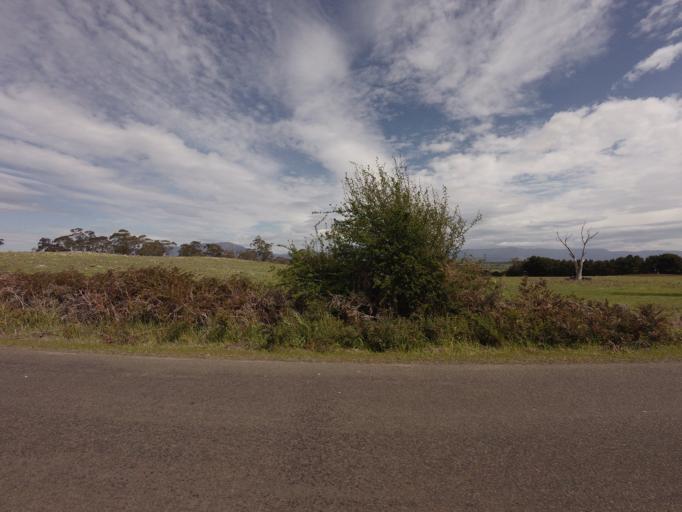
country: AU
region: Tasmania
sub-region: Northern Midlands
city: Longford
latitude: -41.7689
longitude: 147.2154
